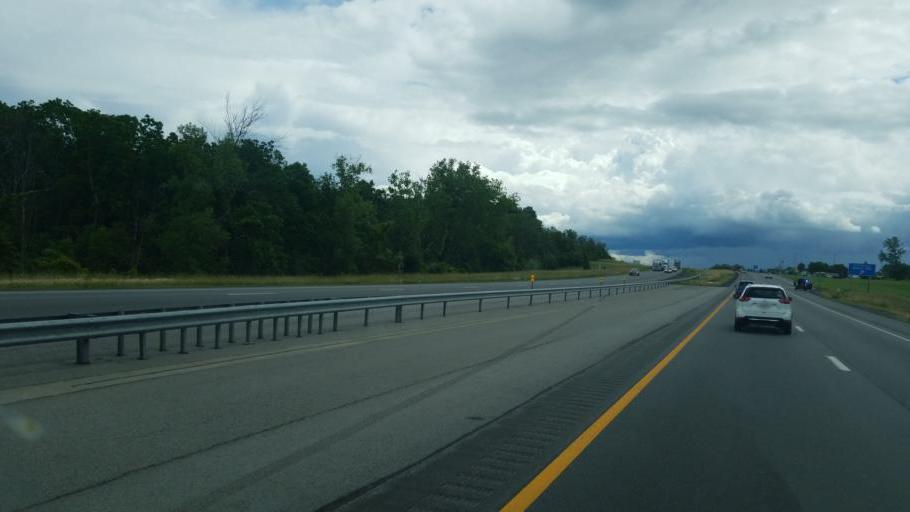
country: US
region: New York
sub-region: Monroe County
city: Scottsville
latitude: 43.0424
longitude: -77.7229
